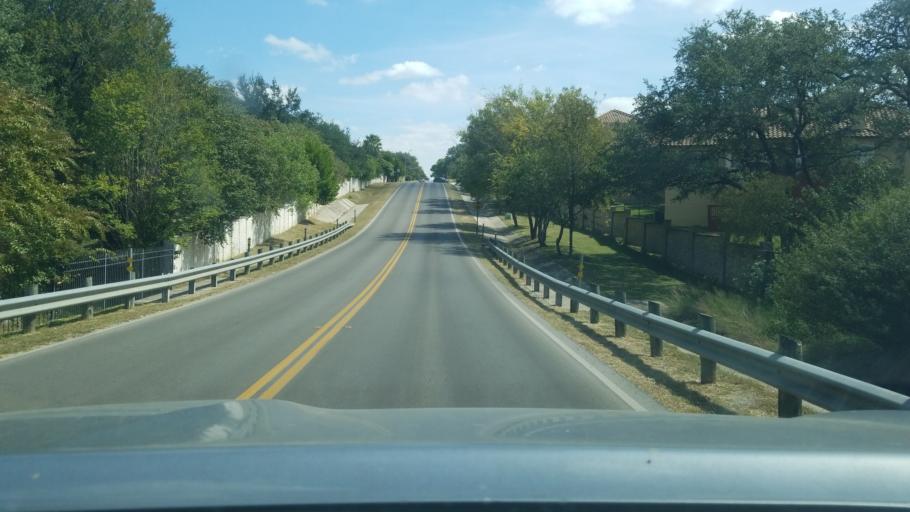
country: US
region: Texas
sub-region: Bexar County
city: Fair Oaks Ranch
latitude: 29.7311
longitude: -98.6446
